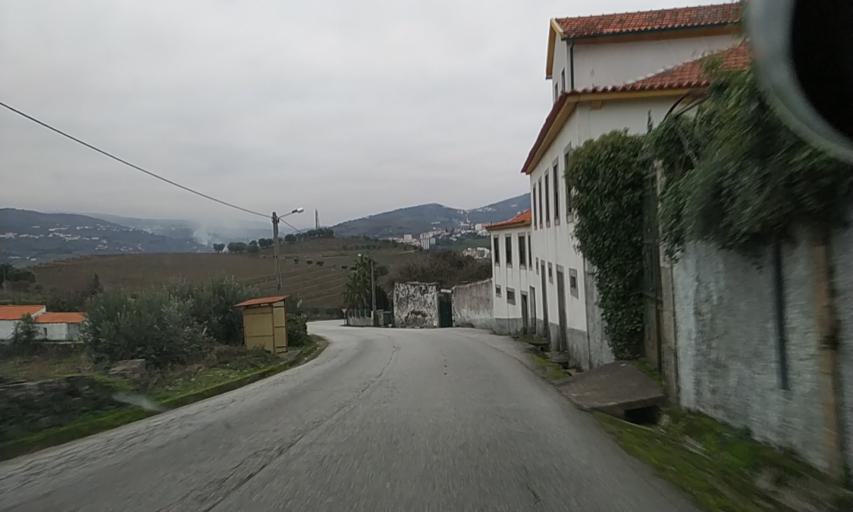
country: PT
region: Vila Real
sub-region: Peso da Regua
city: Peso da Regua
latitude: 41.1516
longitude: -7.7932
